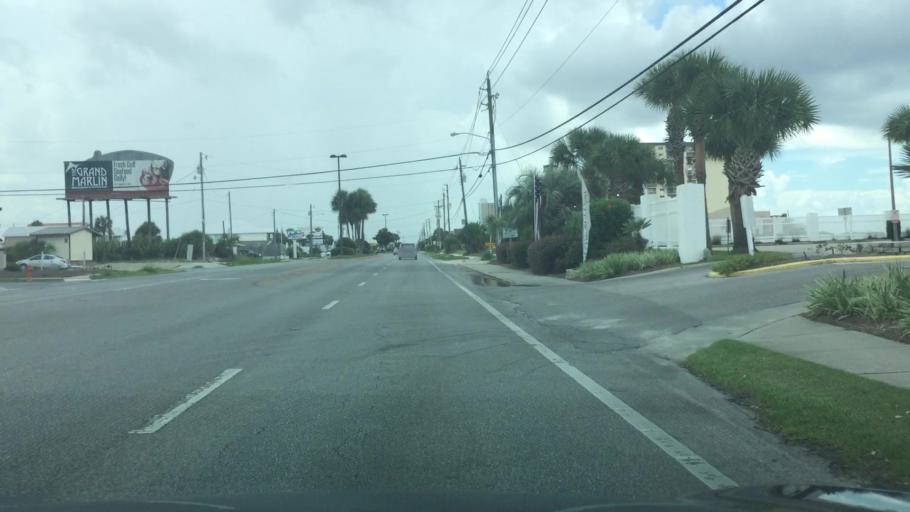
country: US
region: Florida
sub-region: Bay County
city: Lower Grand Lagoon
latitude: 30.1500
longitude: -85.7638
